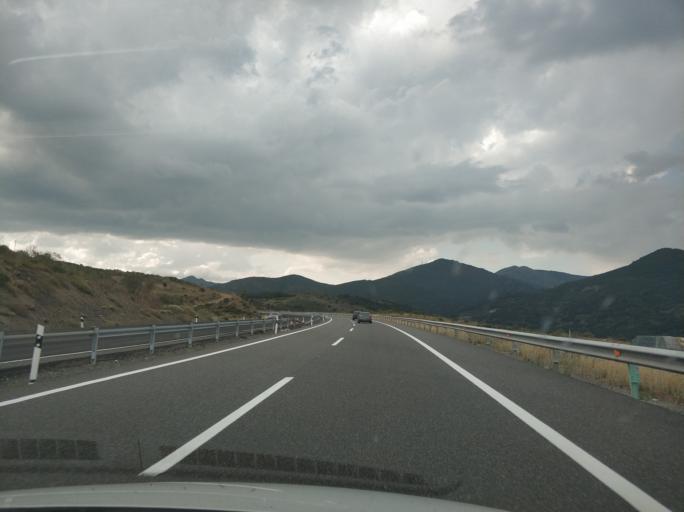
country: ES
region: Castille and Leon
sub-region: Provincia de Leon
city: Soto y Amio
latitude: 42.8066
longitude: -5.8336
